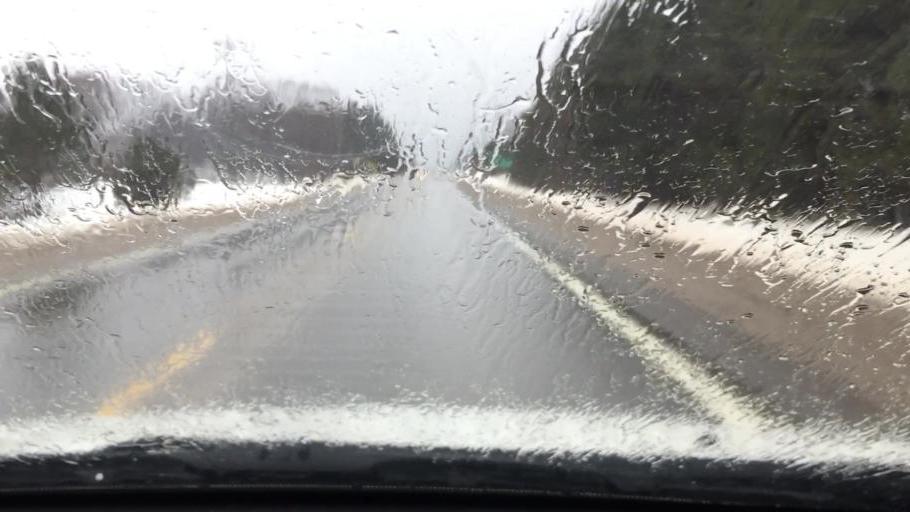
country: US
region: Michigan
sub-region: Charlevoix County
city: Charlevoix
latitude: 45.2703
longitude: -85.2108
